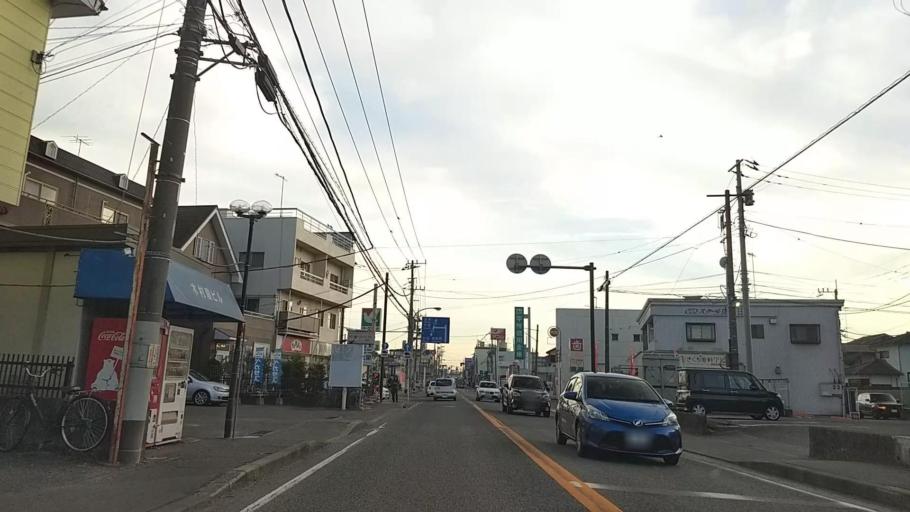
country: JP
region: Kanagawa
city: Atsugi
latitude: 35.4621
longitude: 139.3573
